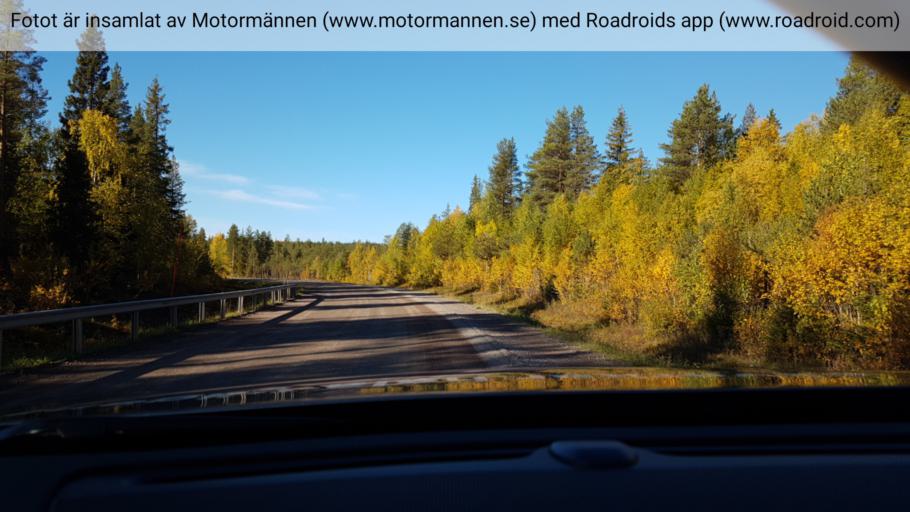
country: SE
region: Norrbotten
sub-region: Alvsbyns Kommun
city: AElvsbyn
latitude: 66.2691
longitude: 20.9907
